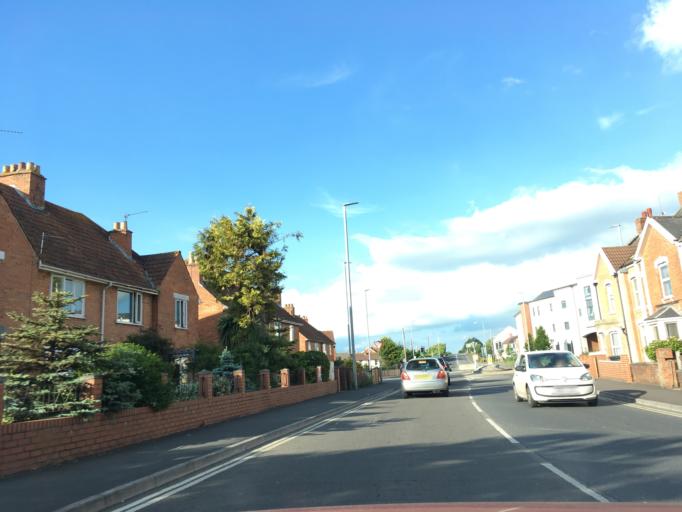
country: GB
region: England
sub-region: Somerset
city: Highbridge
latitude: 51.2235
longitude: -2.9744
